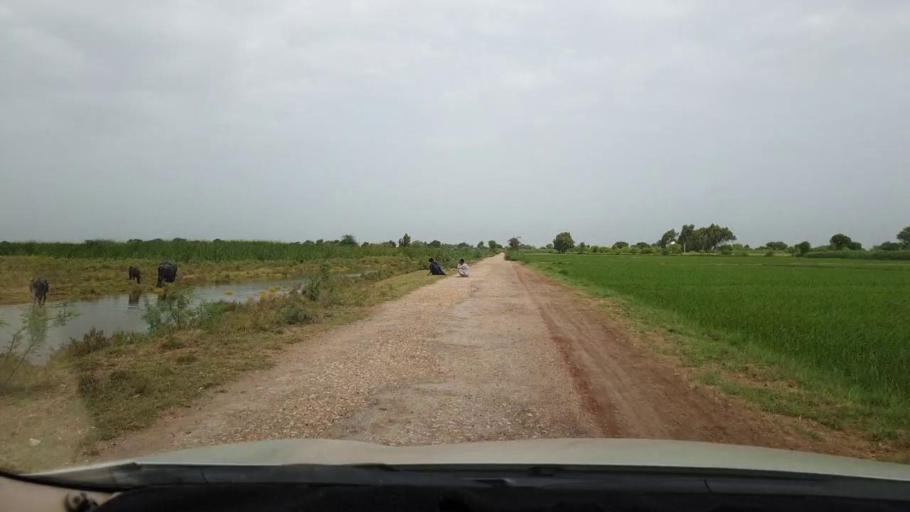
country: PK
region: Sindh
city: Matli
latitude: 25.1055
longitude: 68.6180
